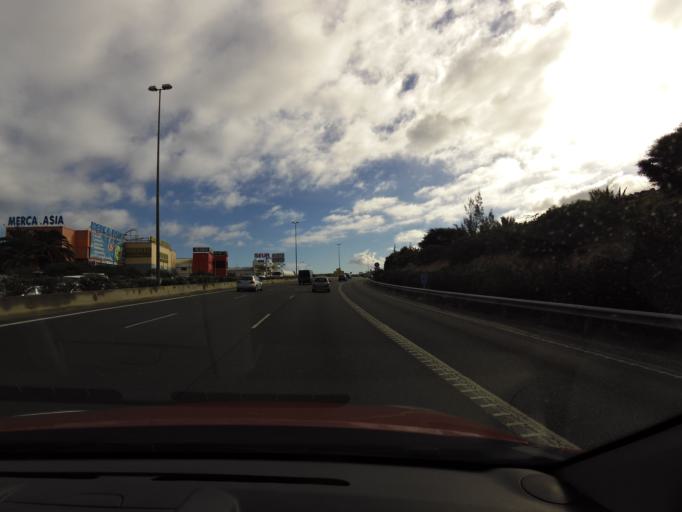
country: ES
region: Canary Islands
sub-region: Provincia de Las Palmas
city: Telde
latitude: 27.9785
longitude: -15.3910
